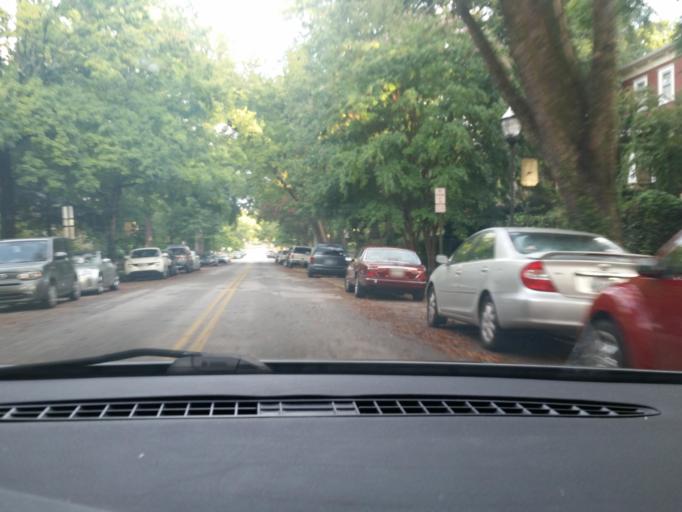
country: US
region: Tennessee
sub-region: Hamilton County
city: Chattanooga
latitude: 35.0440
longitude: -85.2935
